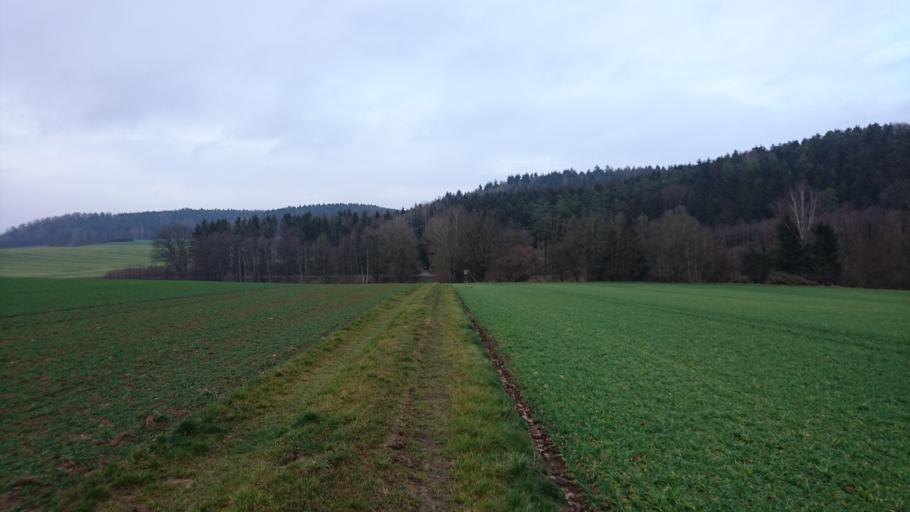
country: DE
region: Bavaria
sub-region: Swabia
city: Altenmunster
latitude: 48.4451
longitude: 10.6046
